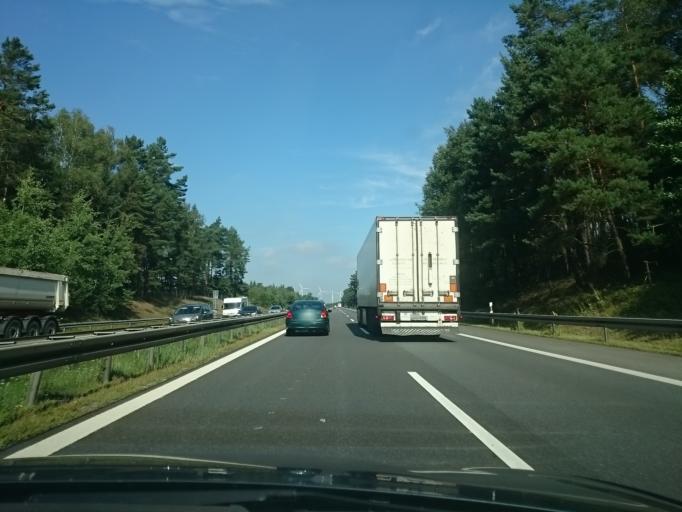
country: DE
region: Brandenburg
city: Bronkow
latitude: 51.7021
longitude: 13.8991
